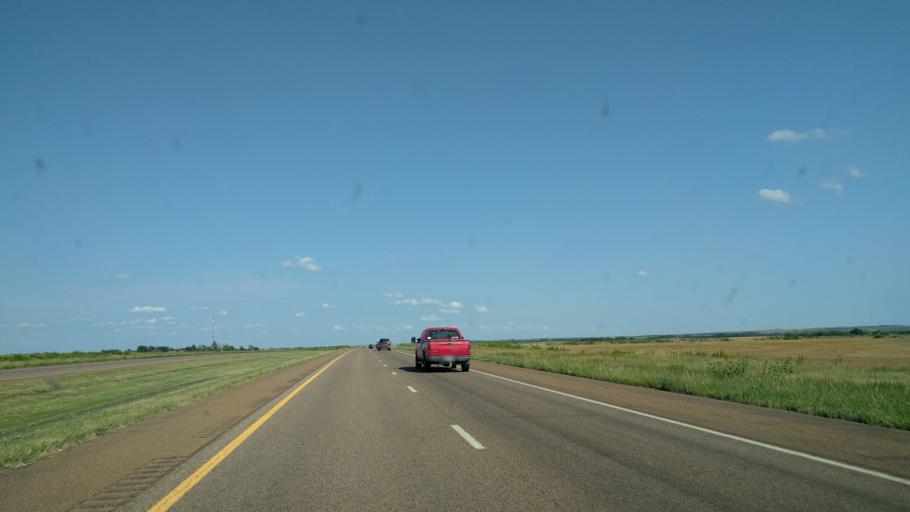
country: US
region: Kansas
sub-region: Ellis County
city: Ellis
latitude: 38.9596
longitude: -99.6250
